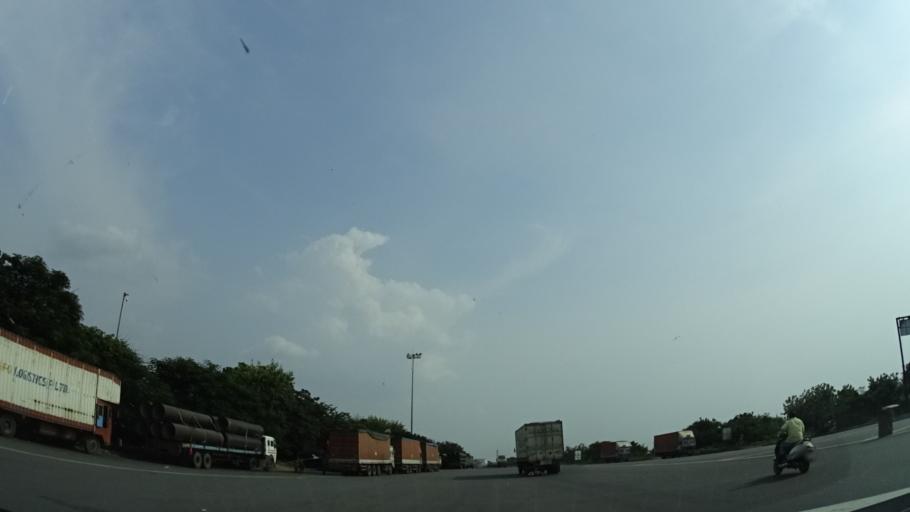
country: IN
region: Telangana
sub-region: Adilabad
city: Nirmal
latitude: 19.0265
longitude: 78.3628
